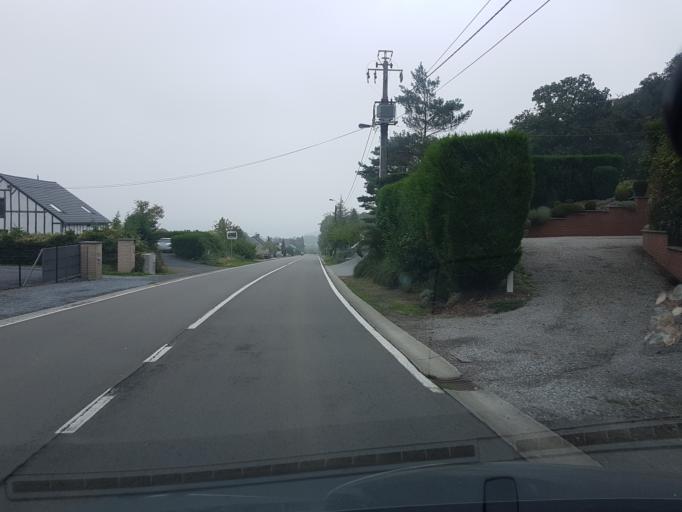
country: BE
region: Wallonia
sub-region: Province de Namur
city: Andenne
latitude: 50.4759
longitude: 5.0982
